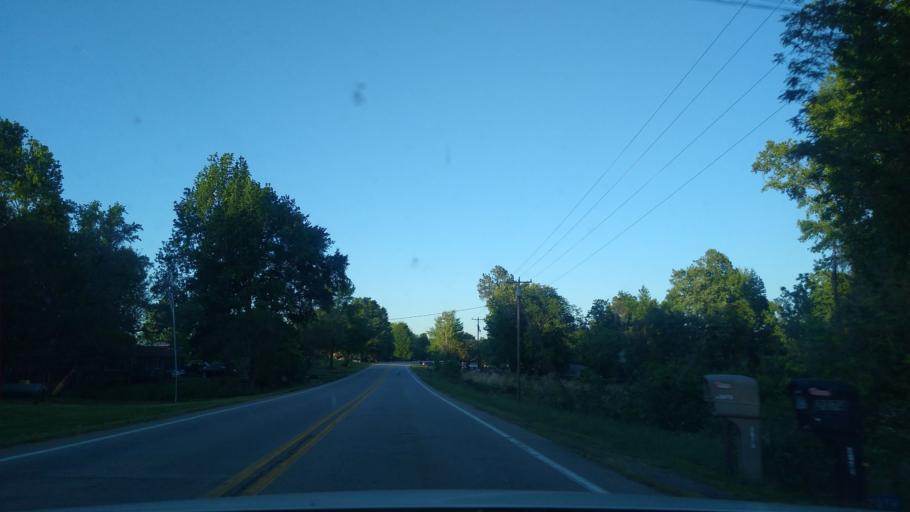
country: US
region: North Carolina
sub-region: Rockingham County
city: Reidsville
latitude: 36.3797
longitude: -79.5809
